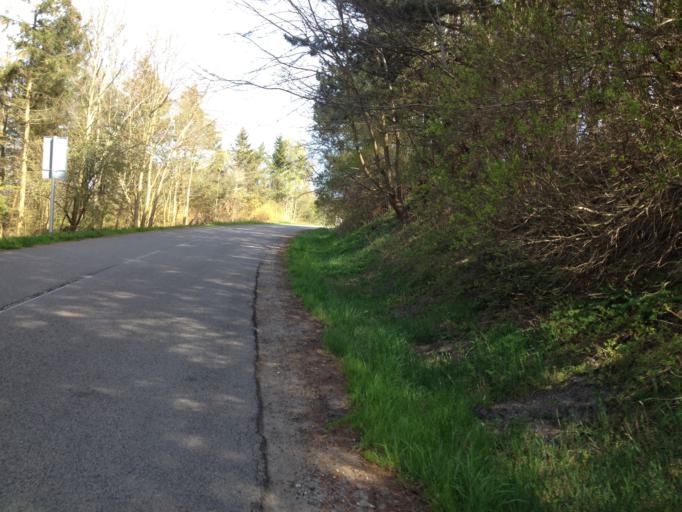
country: DK
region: Capital Region
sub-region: Halsnaes Kommune
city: Hundested
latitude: 55.9514
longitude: 11.8992
